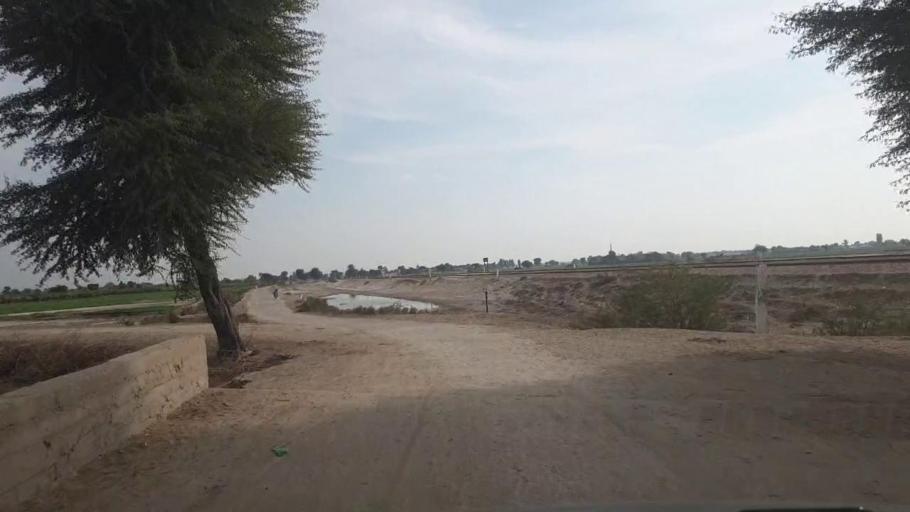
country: PK
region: Sindh
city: Shahpur Chakar
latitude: 26.0869
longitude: 68.4874
